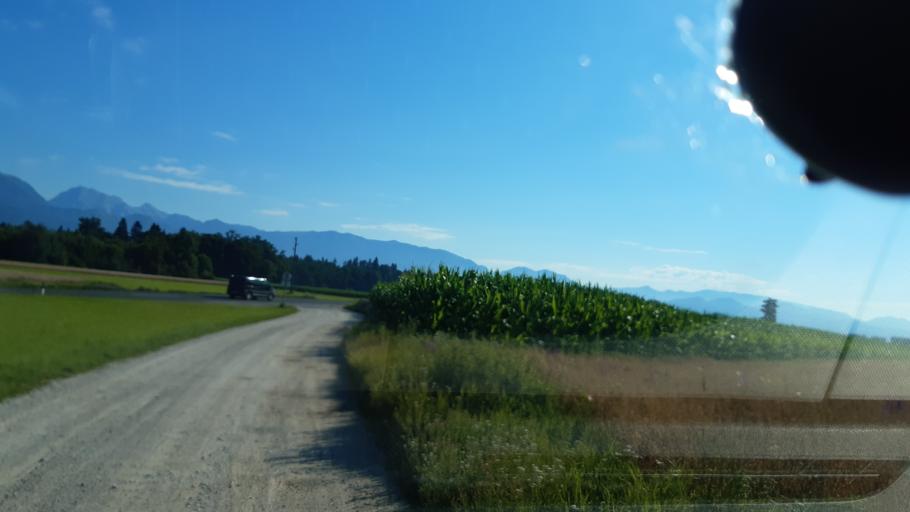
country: SI
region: Vodice
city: Vodice
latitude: 46.1905
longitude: 14.5091
